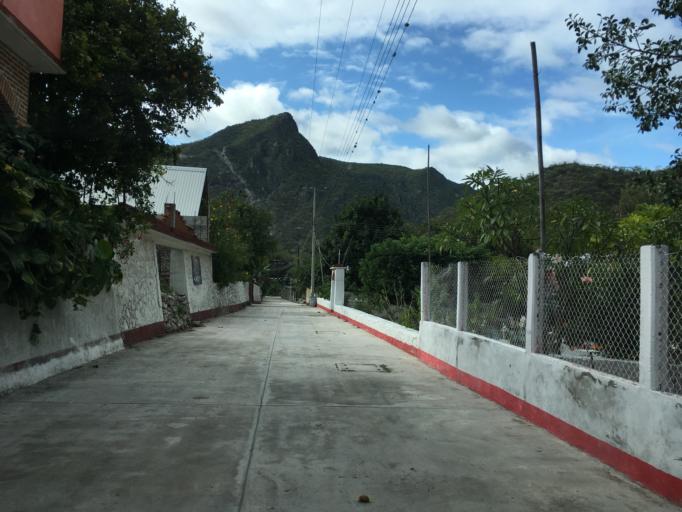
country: MX
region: Hidalgo
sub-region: Metztitlan
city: Fontezuelas
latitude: 20.6398
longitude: -98.9209
